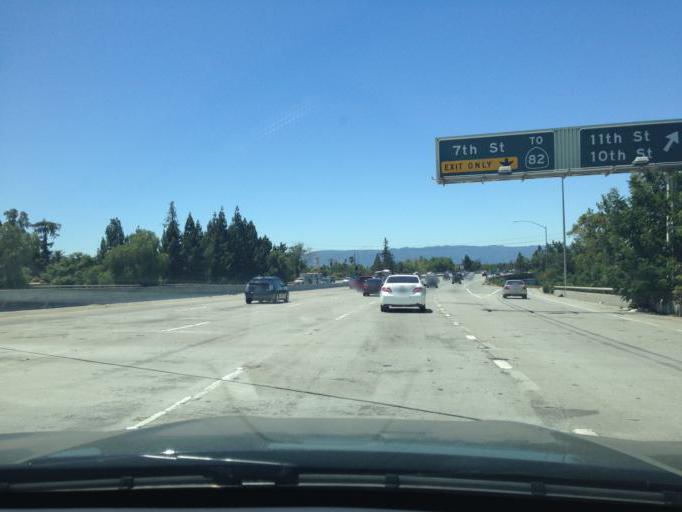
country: US
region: California
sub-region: Santa Clara County
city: San Jose
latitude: 37.3299
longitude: -121.8682
